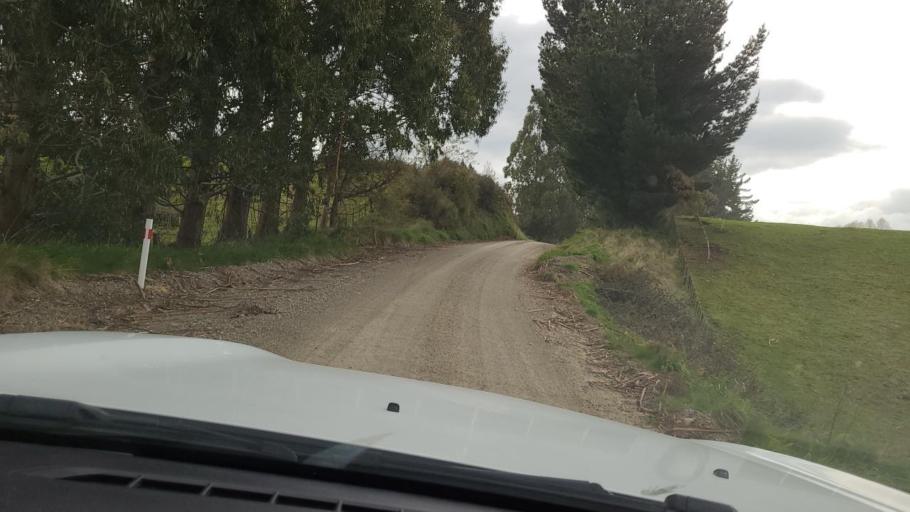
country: NZ
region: Hawke's Bay
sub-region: Napier City
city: Napier
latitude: -39.2606
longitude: 176.8418
